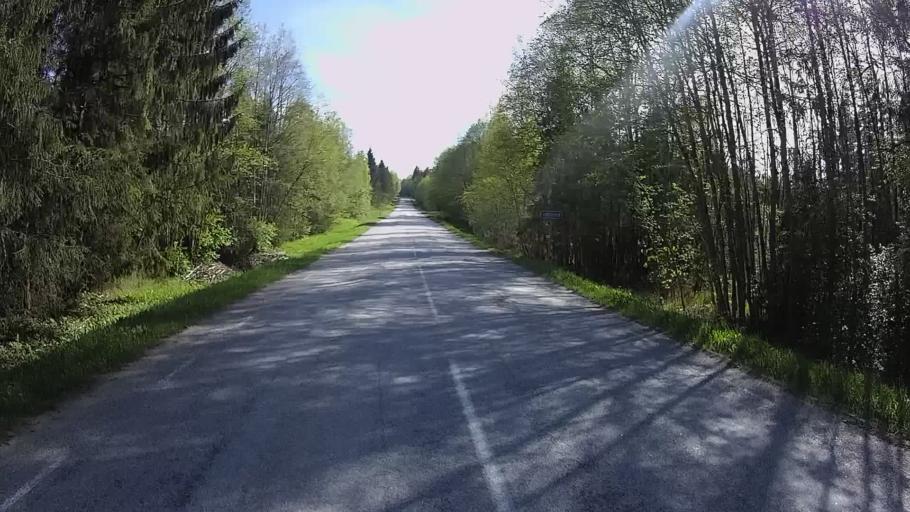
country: EE
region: Vorumaa
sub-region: Antsla vald
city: Vana-Antsla
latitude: 58.0024
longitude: 26.4990
